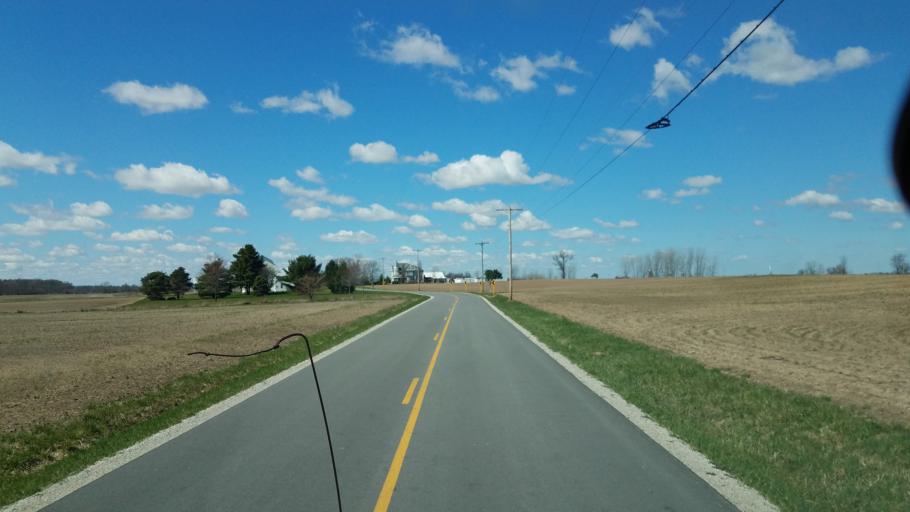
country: US
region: Ohio
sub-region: Seneca County
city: Fostoria
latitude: 41.1573
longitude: -83.4606
